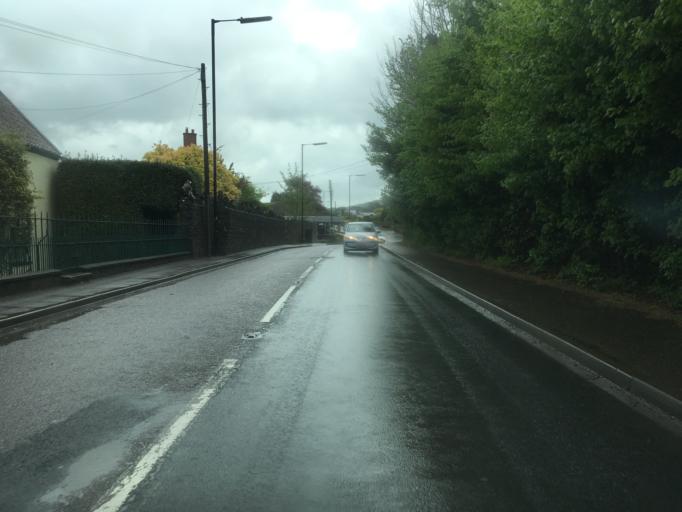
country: GB
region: England
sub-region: North Somerset
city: Sandford
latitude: 51.3326
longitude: -2.8321
